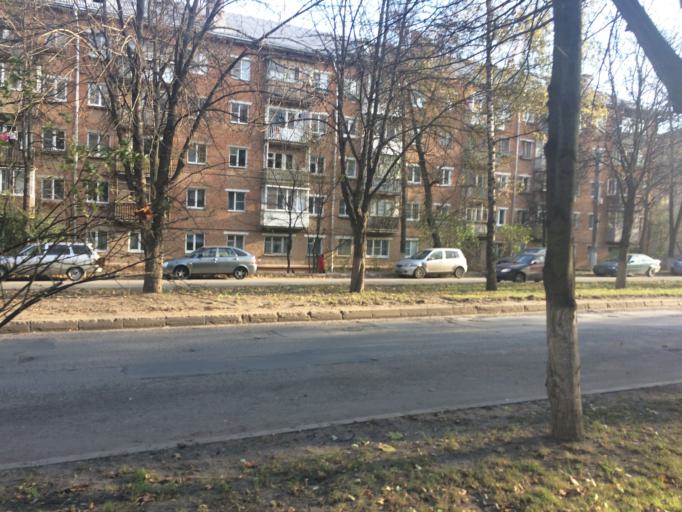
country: RU
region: Tula
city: Mendeleyevskiy
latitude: 54.1603
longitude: 37.5894
